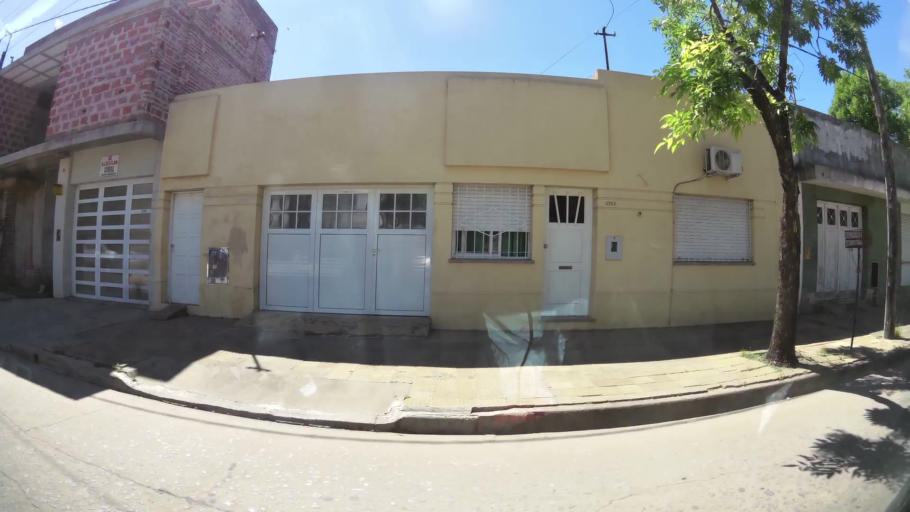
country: AR
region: Santa Fe
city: Esperanza
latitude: -31.4441
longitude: -60.9267
